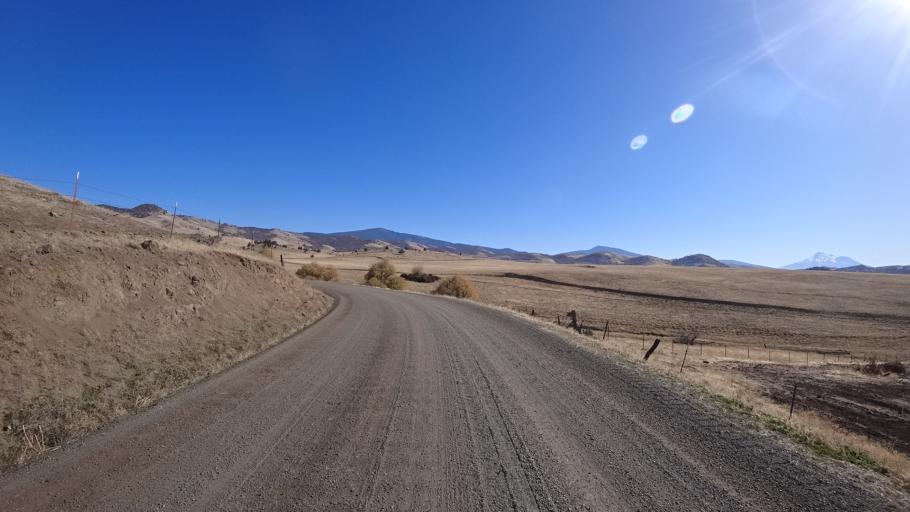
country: US
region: California
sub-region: Siskiyou County
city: Montague
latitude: 41.8311
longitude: -122.3870
